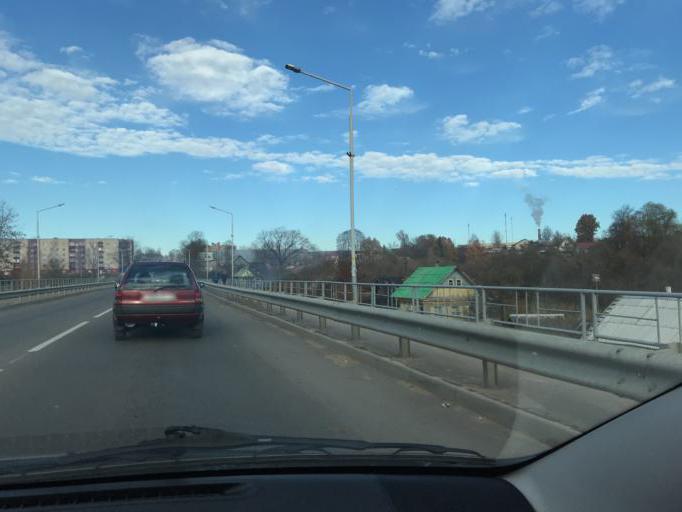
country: BY
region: Vitebsk
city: Haradok
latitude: 55.4668
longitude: 29.9771
